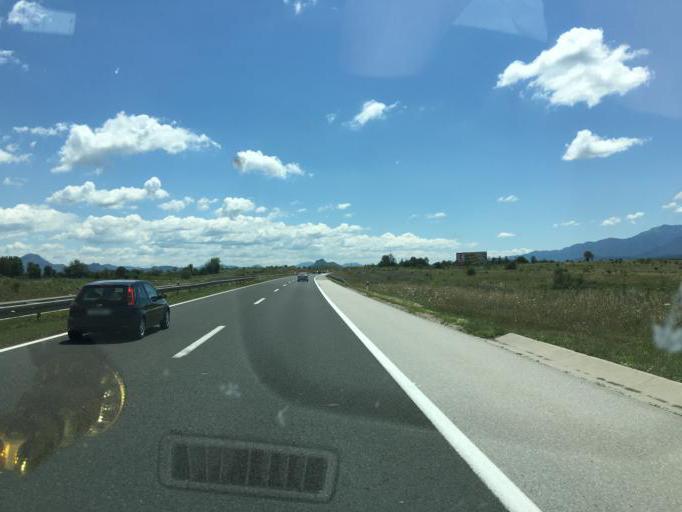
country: HR
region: Licko-Senjska
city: Gospic
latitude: 44.5031
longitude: 15.5288
